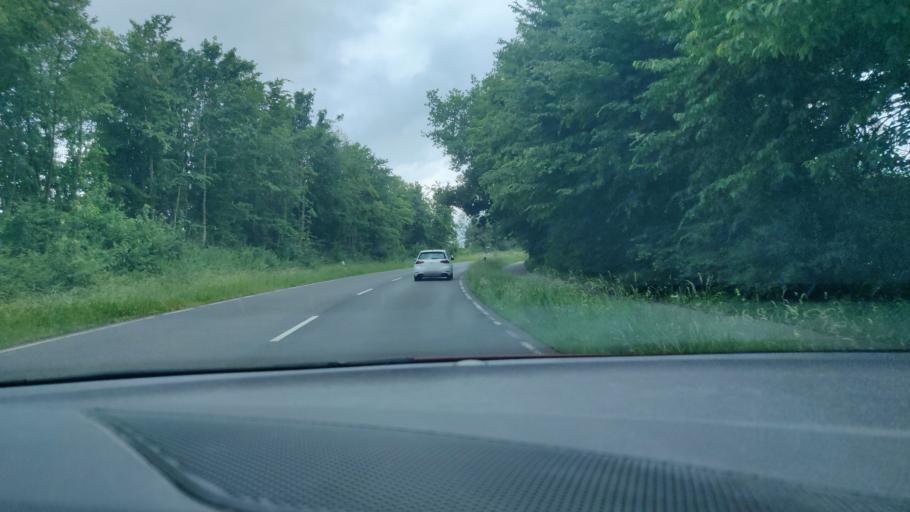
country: DE
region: North Rhine-Westphalia
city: Wulfrath
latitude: 51.2929
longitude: 7.0870
